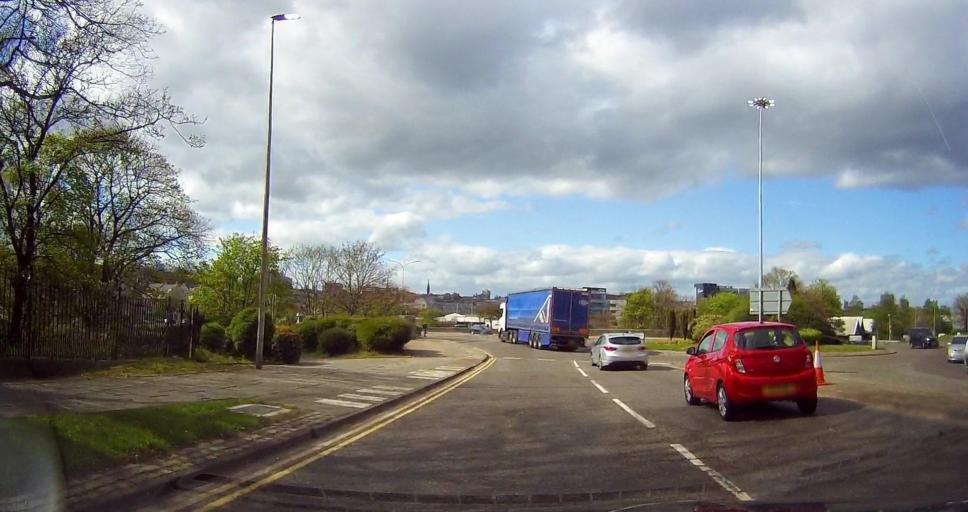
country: GB
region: Scotland
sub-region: Aberdeen City
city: Aberdeen
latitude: 57.1351
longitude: -2.0937
